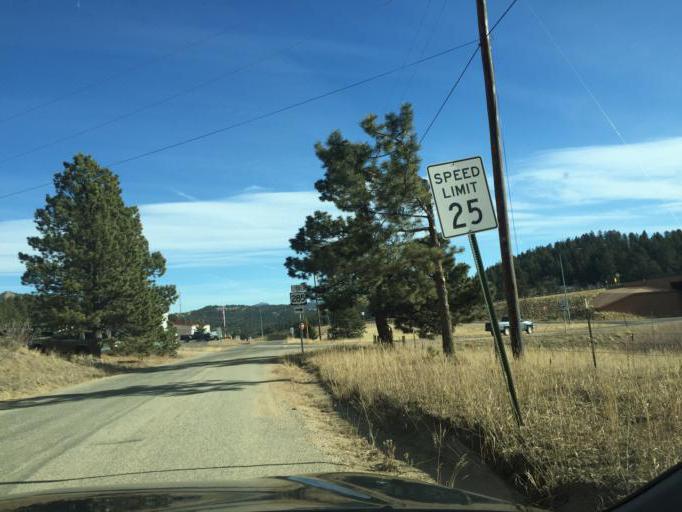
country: US
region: Colorado
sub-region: Jefferson County
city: Evergreen
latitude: 39.4361
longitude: -105.4628
